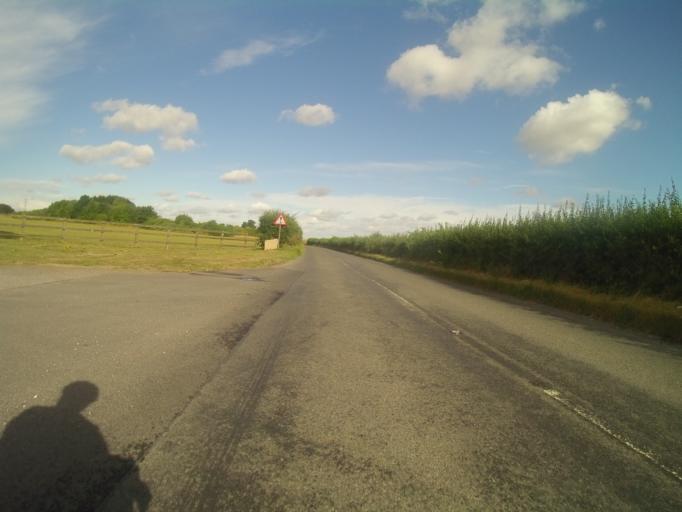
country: GB
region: England
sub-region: Wiltshire
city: Bulford
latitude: 51.1860
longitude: -1.7461
